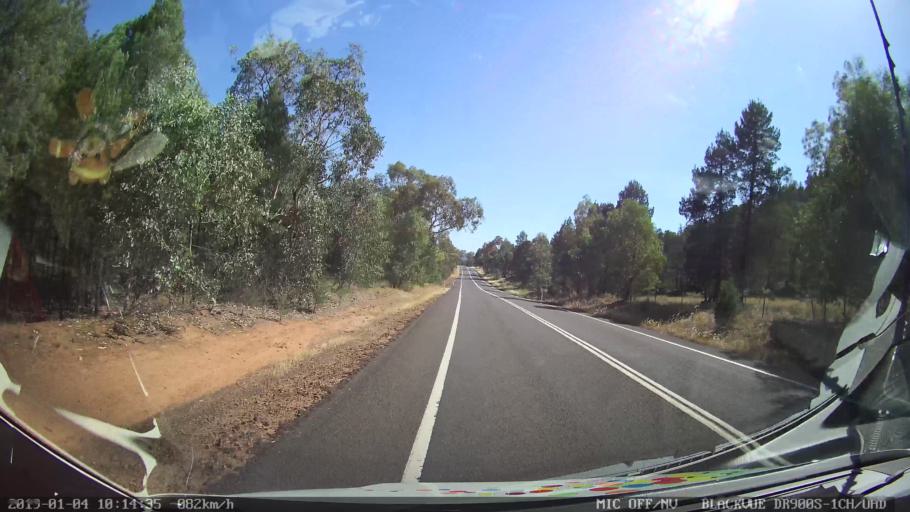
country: AU
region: New South Wales
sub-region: Cabonne
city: Canowindra
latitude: -33.3955
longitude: 148.4146
